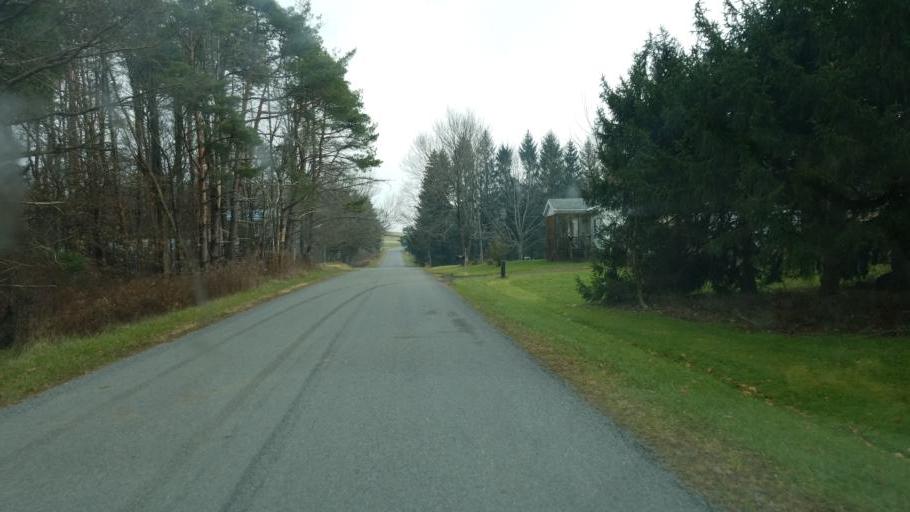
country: US
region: Pennsylvania
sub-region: Crawford County
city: Cochranton
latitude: 41.5038
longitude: -80.1010
